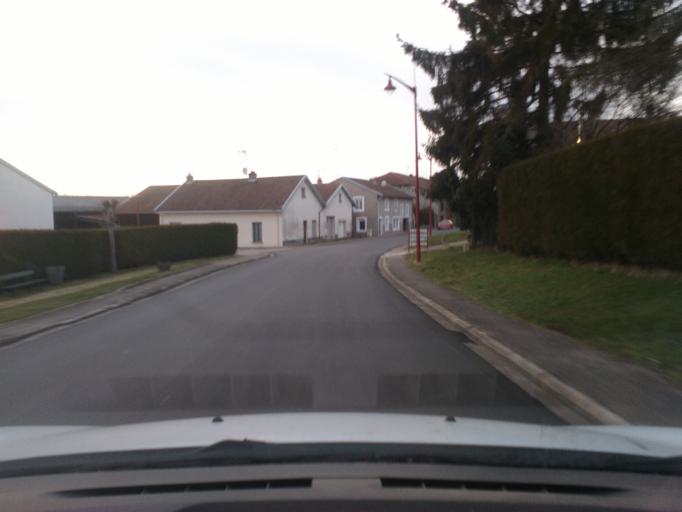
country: FR
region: Lorraine
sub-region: Departement des Vosges
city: Vincey
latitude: 48.3593
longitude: 6.3260
